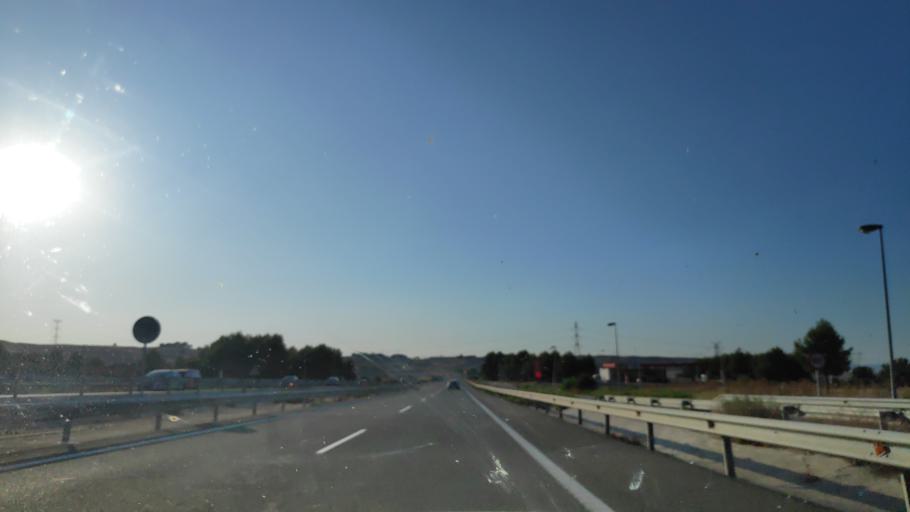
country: ES
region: Castille-La Mancha
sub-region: Provincia de Cuenca
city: Belinchon
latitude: 40.0311
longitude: -3.0396
